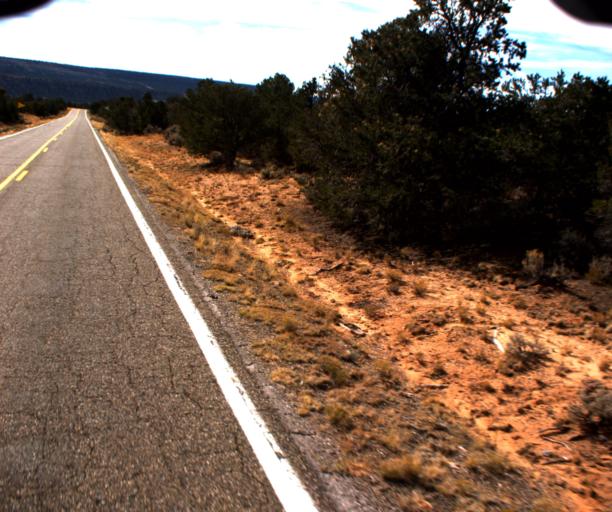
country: US
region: Arizona
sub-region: Navajo County
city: Kayenta
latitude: 36.5828
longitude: -110.4908
